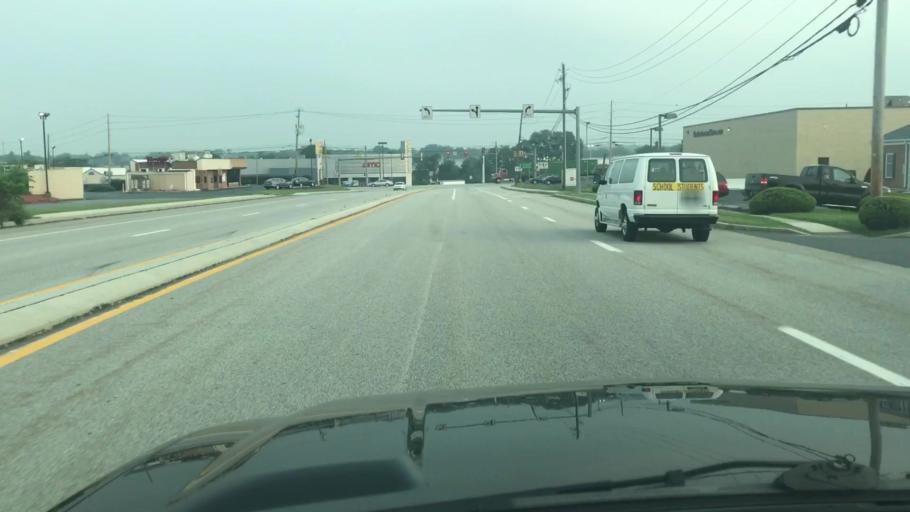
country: US
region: Pennsylvania
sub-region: Cumberland County
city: Shiremanstown
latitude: 40.2248
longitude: -76.9383
